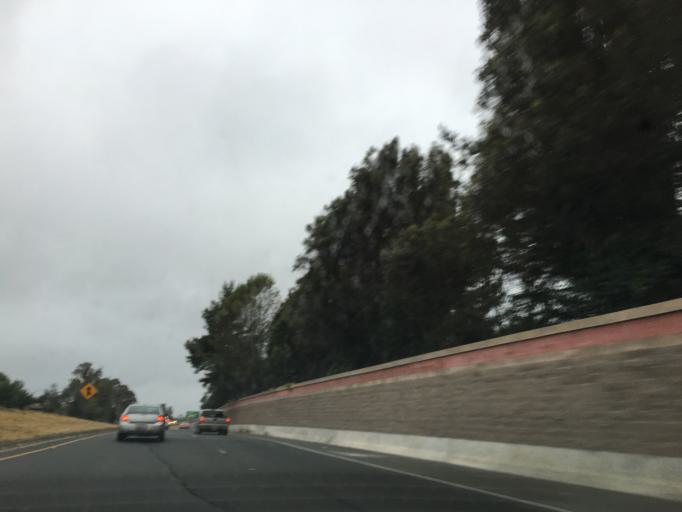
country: US
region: California
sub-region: Sonoma County
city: Santa Rosa
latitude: 38.4364
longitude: -122.6889
